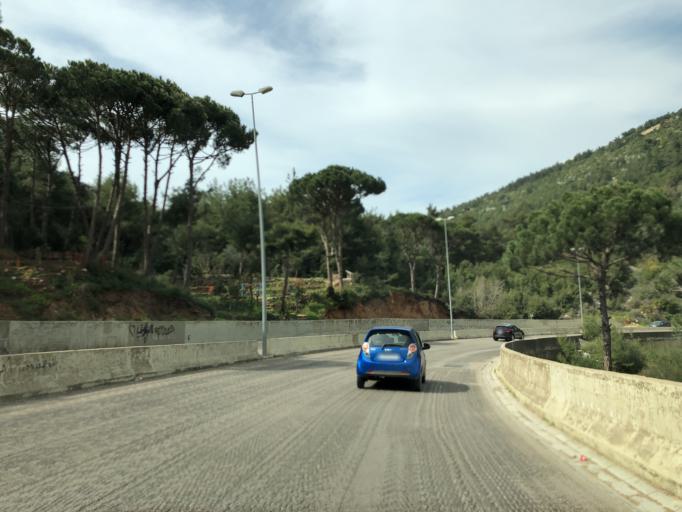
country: LB
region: Mont-Liban
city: Bhamdoun el Mhatta
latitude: 33.8924
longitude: 35.6575
